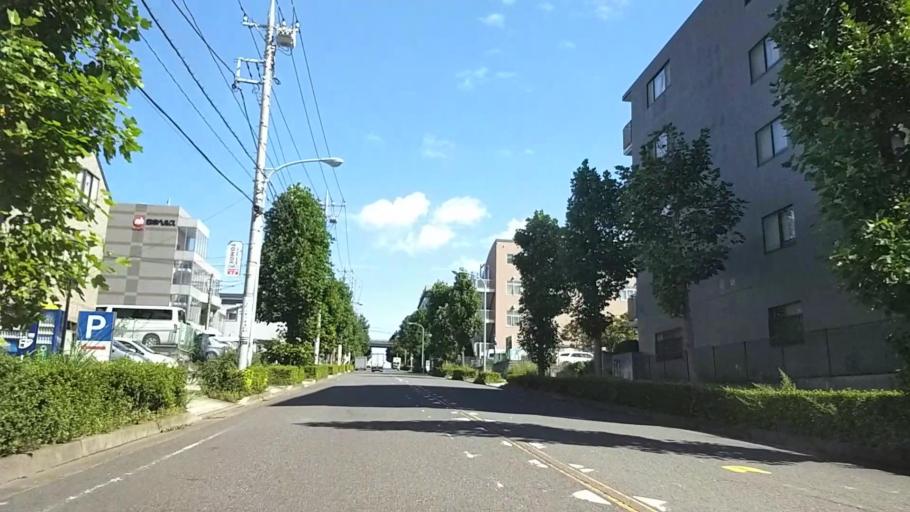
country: JP
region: Tokyo
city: Chofugaoka
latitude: 35.5634
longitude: 139.5532
